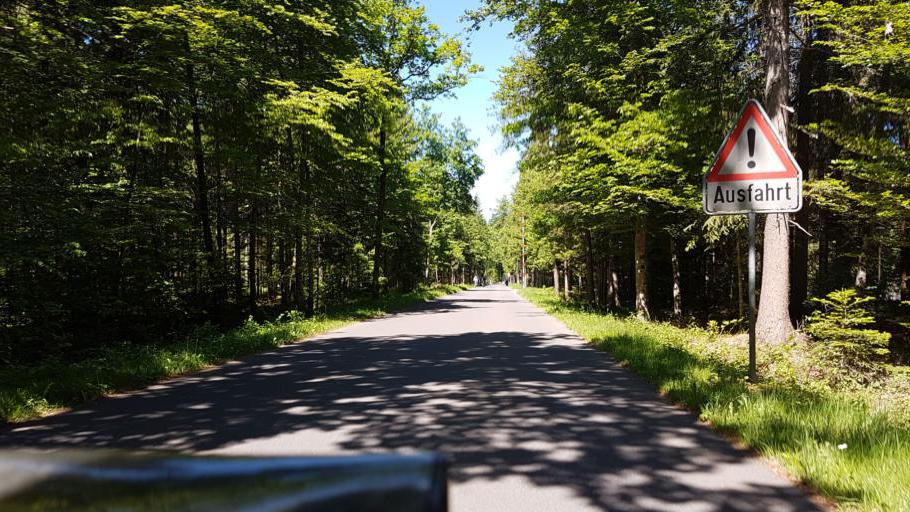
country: CH
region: Bern
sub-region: Thun District
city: Thun
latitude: 46.7277
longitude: 7.5980
